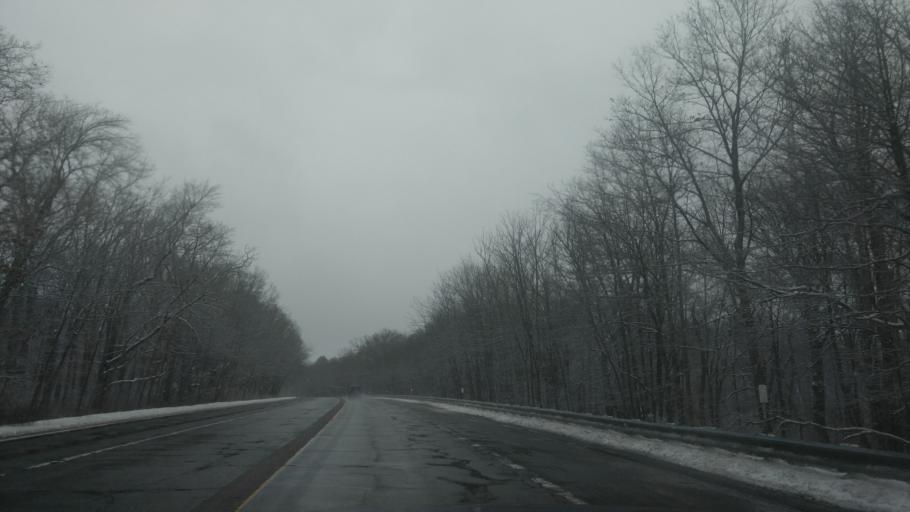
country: US
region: Rhode Island
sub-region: Providence County
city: North Scituate
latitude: 41.8276
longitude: -71.6631
